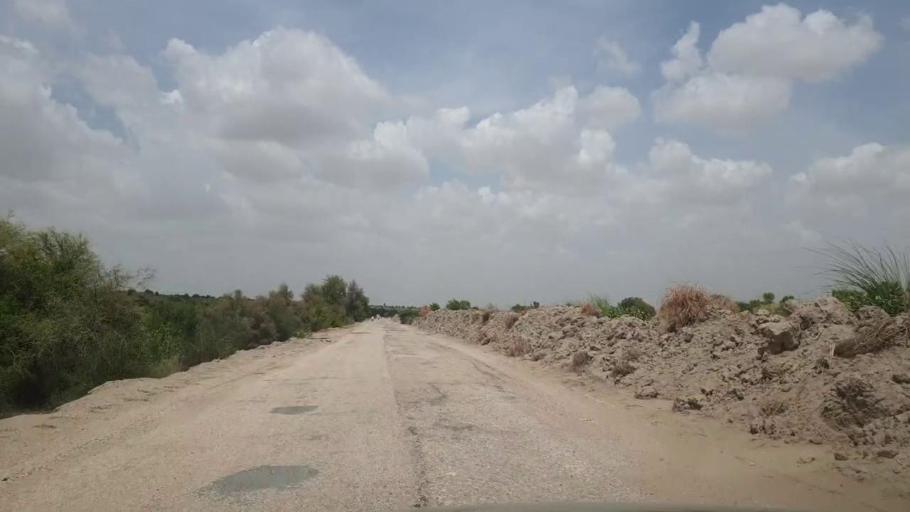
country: PK
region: Sindh
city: Kot Diji
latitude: 27.2144
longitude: 69.0993
